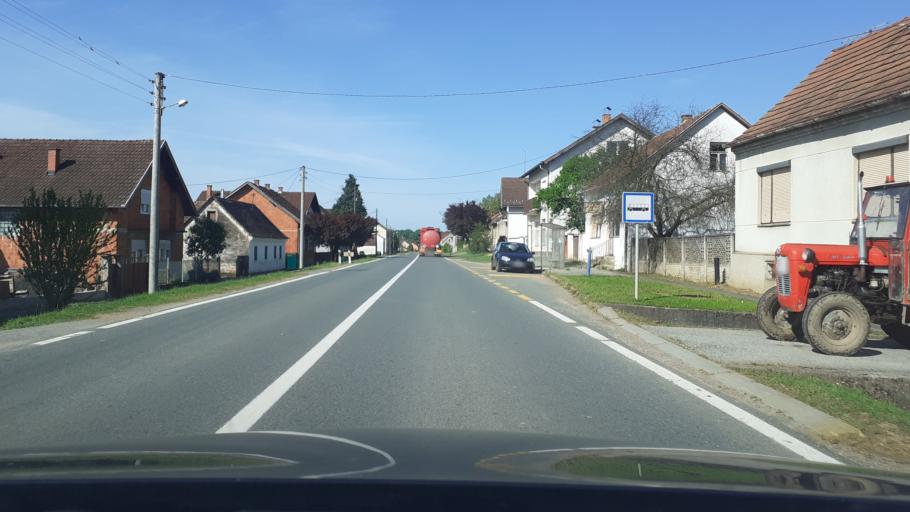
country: HR
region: Brodsko-Posavska
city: Batrina
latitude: 45.2137
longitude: 17.6946
